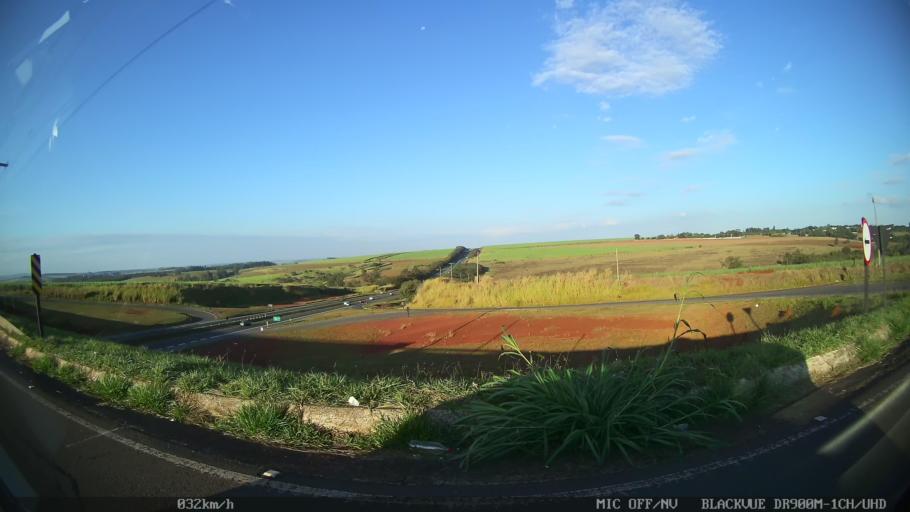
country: BR
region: Sao Paulo
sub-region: Piracicaba
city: Piracicaba
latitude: -22.7247
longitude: -47.5847
